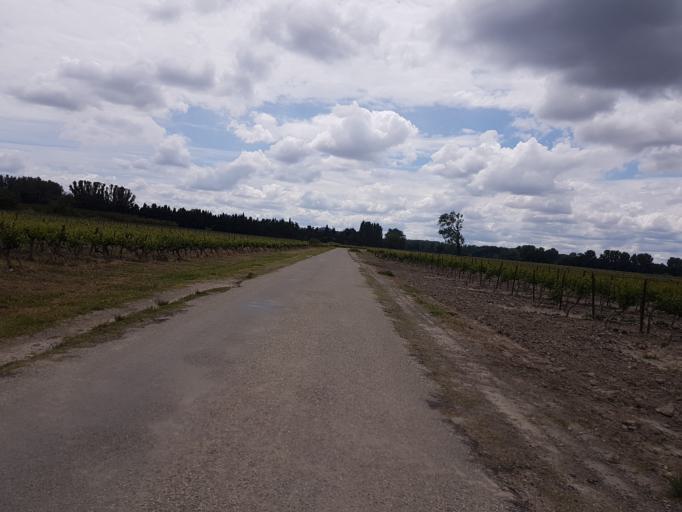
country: FR
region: Languedoc-Roussillon
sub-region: Departement du Gard
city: Vallabregues
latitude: 43.8745
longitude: 4.6252
